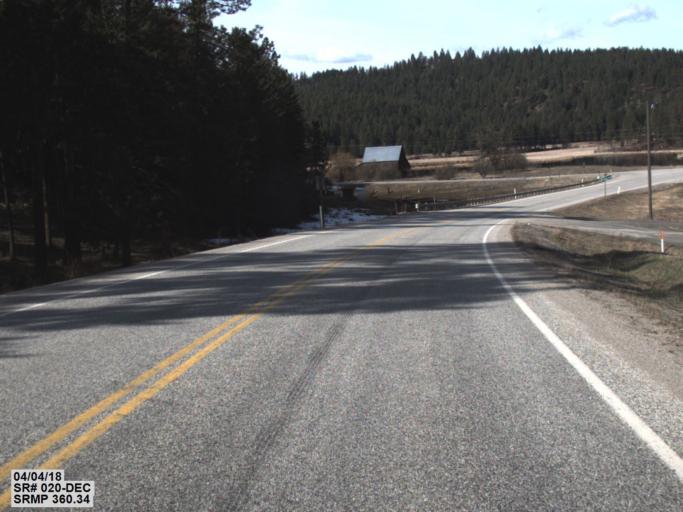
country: US
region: Washington
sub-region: Stevens County
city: Colville
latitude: 48.5144
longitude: -117.8020
